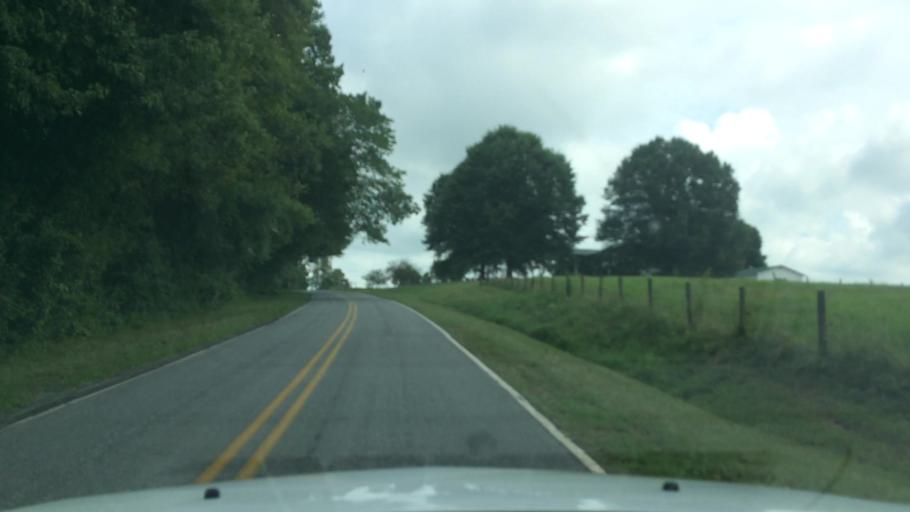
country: US
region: North Carolina
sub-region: Yadkin County
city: Jonesville
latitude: 36.1095
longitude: -80.8564
